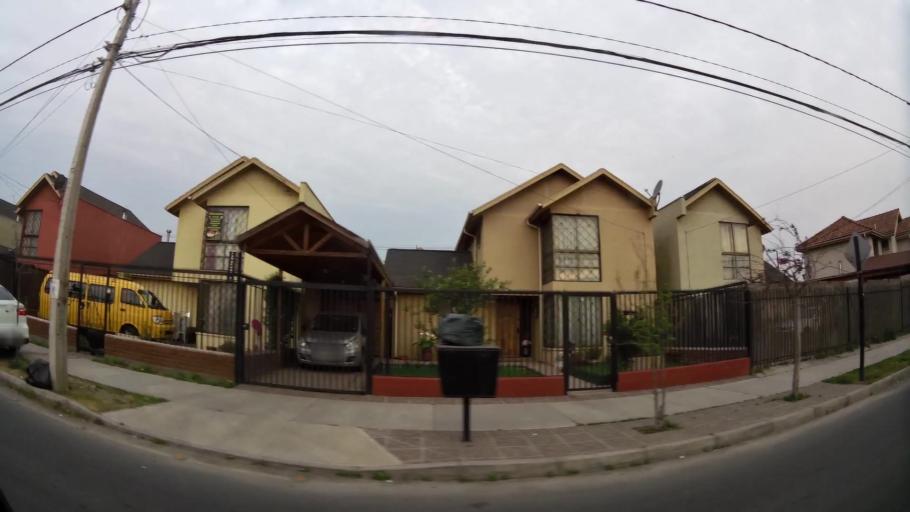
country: CL
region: Santiago Metropolitan
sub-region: Provincia de Santiago
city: Lo Prado
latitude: -33.5297
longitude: -70.7925
